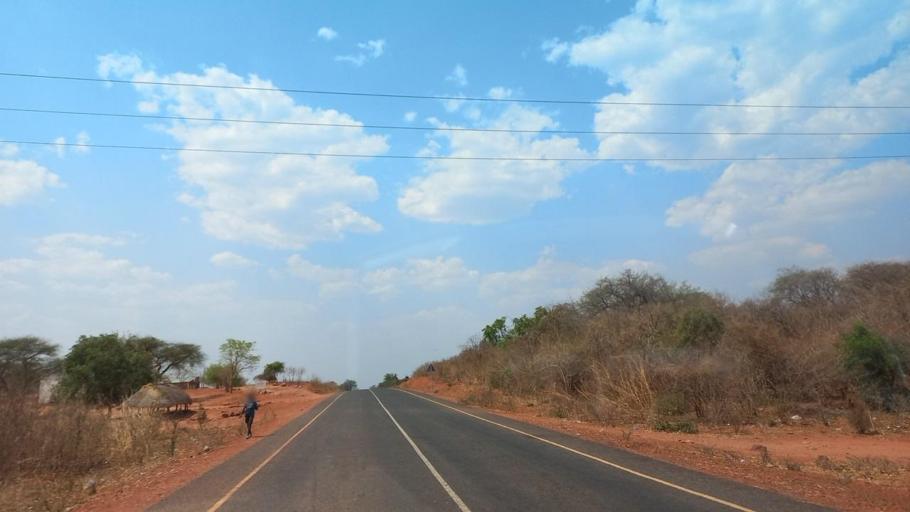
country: ZM
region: Lusaka
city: Luangwa
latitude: -15.4137
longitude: 30.3706
